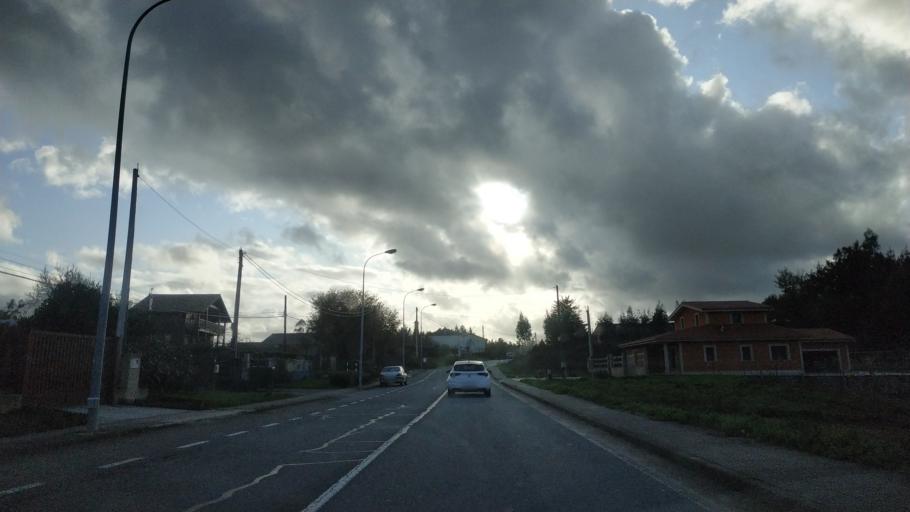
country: ES
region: Galicia
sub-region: Provincia da Coruna
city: Arzua
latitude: 42.9179
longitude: -8.1664
